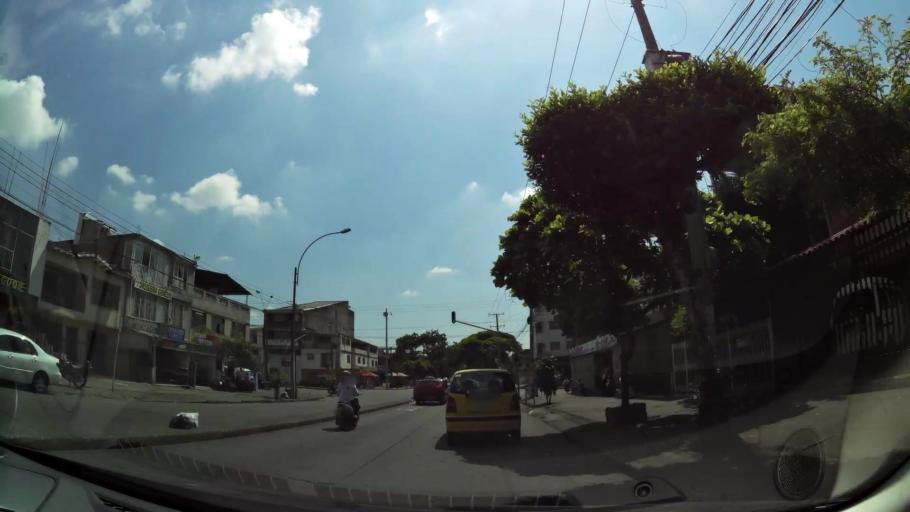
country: CO
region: Valle del Cauca
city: Cali
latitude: 3.4360
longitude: -76.5265
